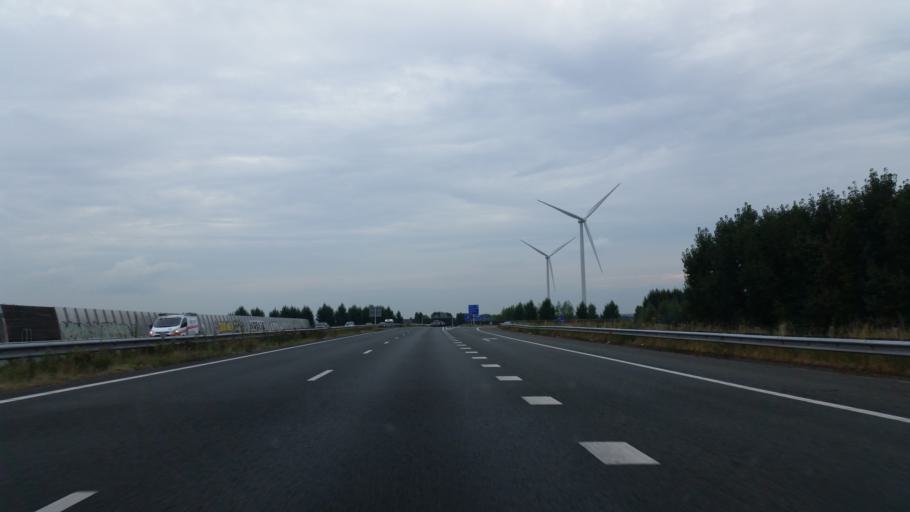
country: NL
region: Gelderland
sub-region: Gemeente Ede
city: Ede
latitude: 52.0393
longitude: 5.6176
